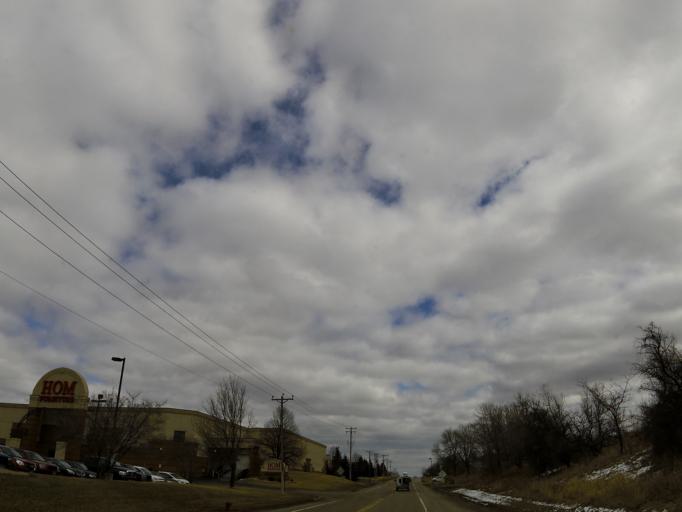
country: US
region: Minnesota
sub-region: Washington County
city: Oakdale
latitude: 44.9474
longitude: -92.9534
